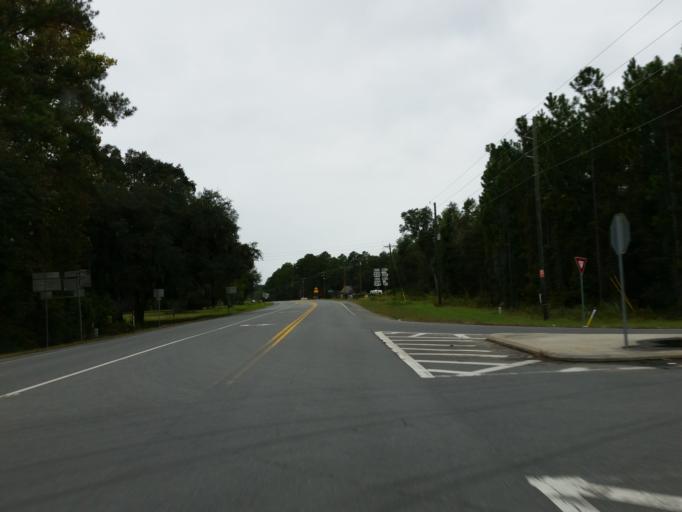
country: US
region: Georgia
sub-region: Lanier County
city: Lakeland
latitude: 31.0479
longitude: -83.0316
